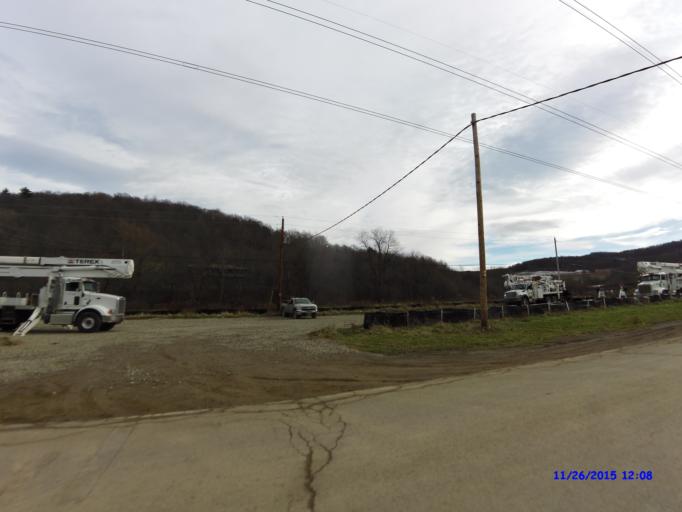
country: US
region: New York
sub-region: Cattaraugus County
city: Allegany
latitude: 42.1940
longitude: -78.4632
